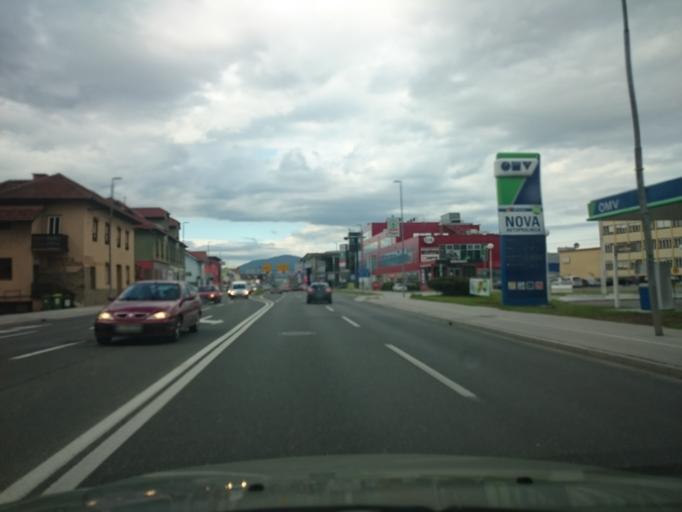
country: SI
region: Celje
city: Celje
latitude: 46.2393
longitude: 15.2742
